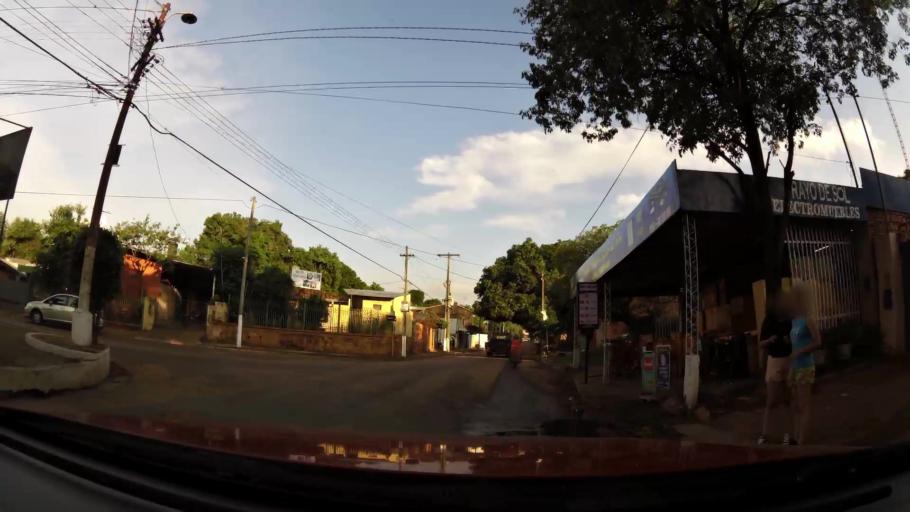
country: PY
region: Central
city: Fernando de la Mora
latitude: -25.3552
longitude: -57.5174
